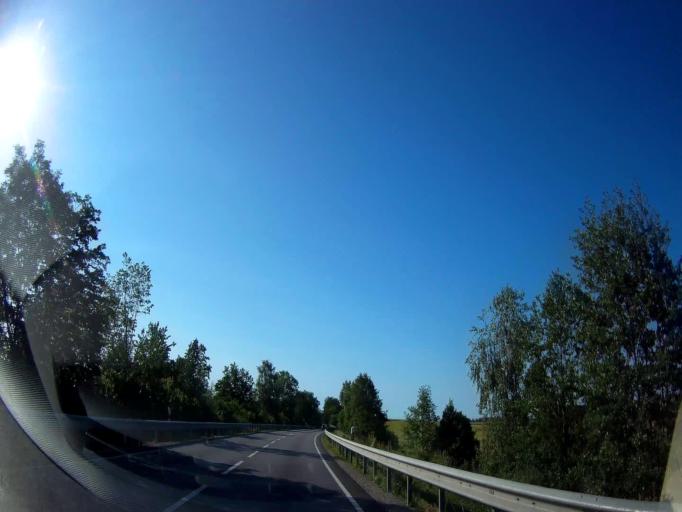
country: DE
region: Bavaria
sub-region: Lower Bavaria
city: Wurmannsquick
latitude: 48.3533
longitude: 12.7977
